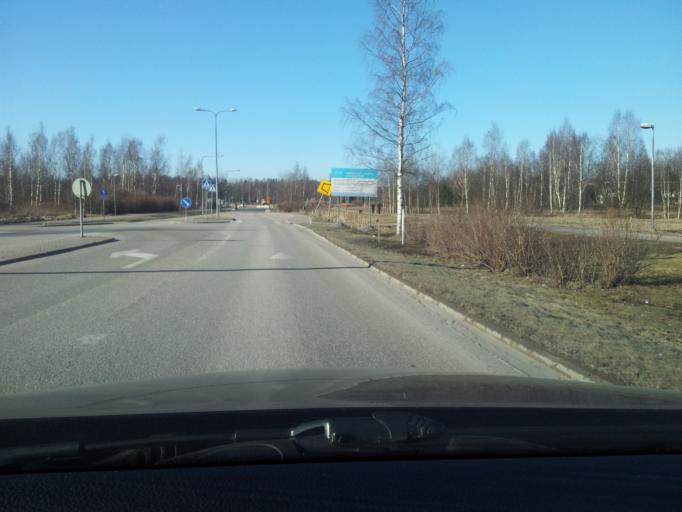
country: FI
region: Uusimaa
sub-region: Helsinki
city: Koukkuniemi
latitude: 60.1825
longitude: 24.7787
